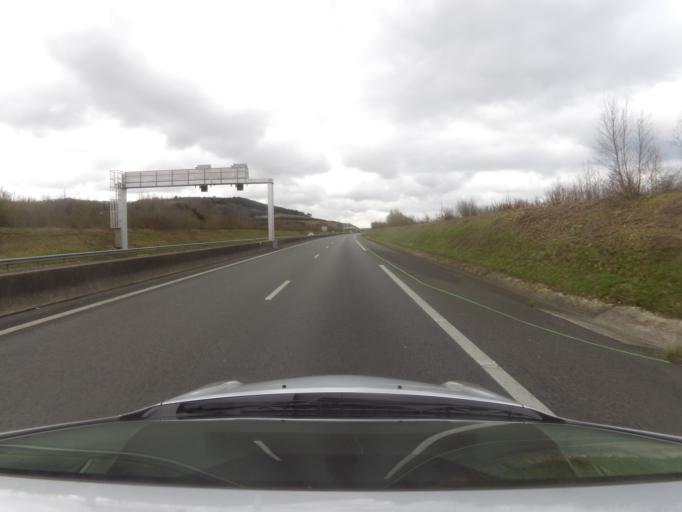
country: FR
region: Nord-Pas-de-Calais
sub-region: Departement du Pas-de-Calais
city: Nesles
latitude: 50.6312
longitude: 1.6644
